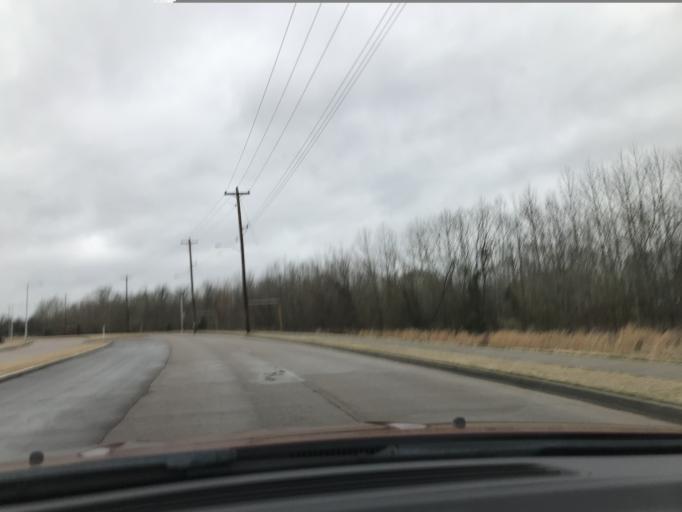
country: US
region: Tennessee
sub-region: Shelby County
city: Collierville
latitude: 35.0814
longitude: -89.6835
